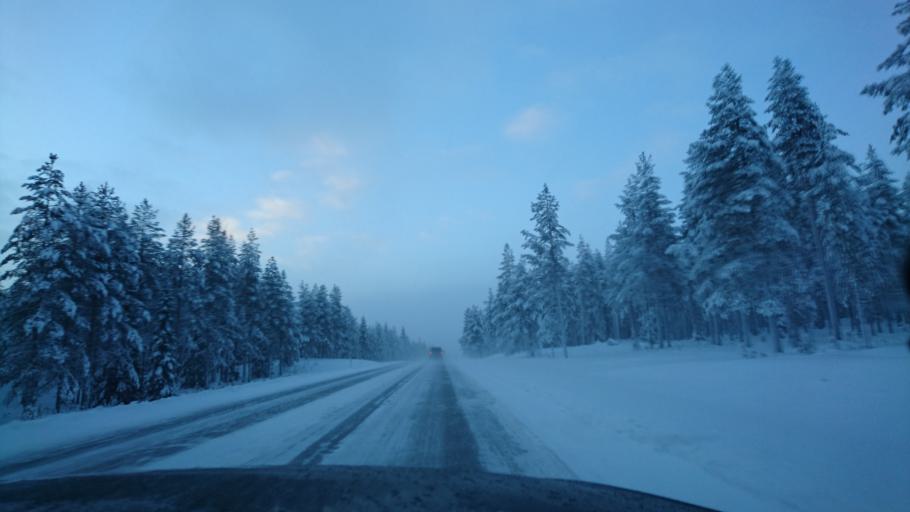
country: FI
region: Northern Ostrobothnia
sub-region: Koillismaa
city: Taivalkoski
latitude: 65.4800
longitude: 27.7970
